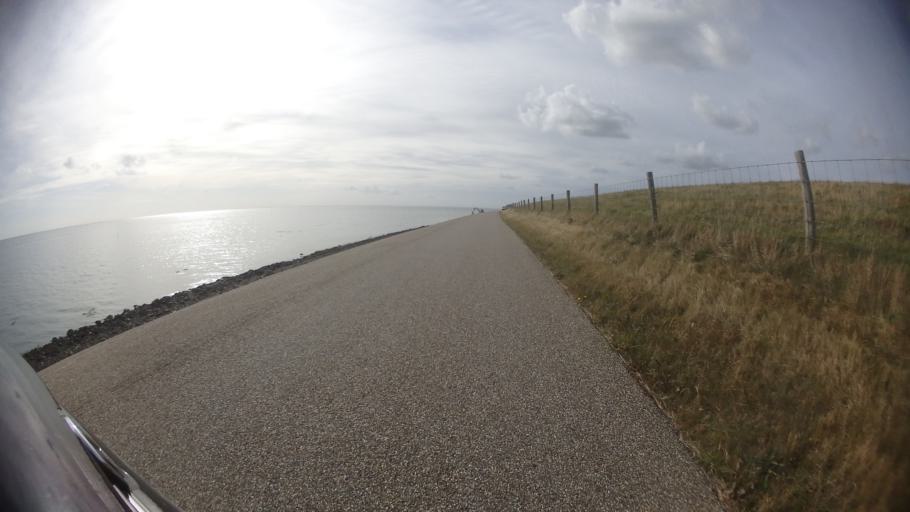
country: NL
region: North Holland
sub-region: Gemeente Texel
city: Den Burg
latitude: 53.0832
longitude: 4.8994
